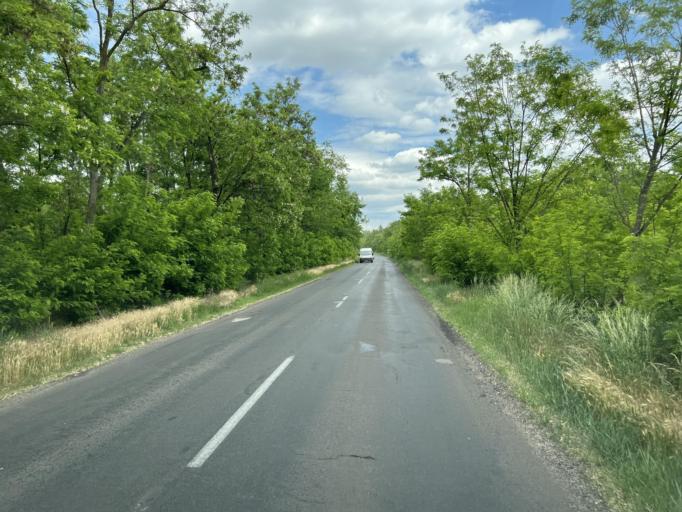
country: HU
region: Pest
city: Tapioszecso
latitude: 47.4685
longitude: 19.6174
